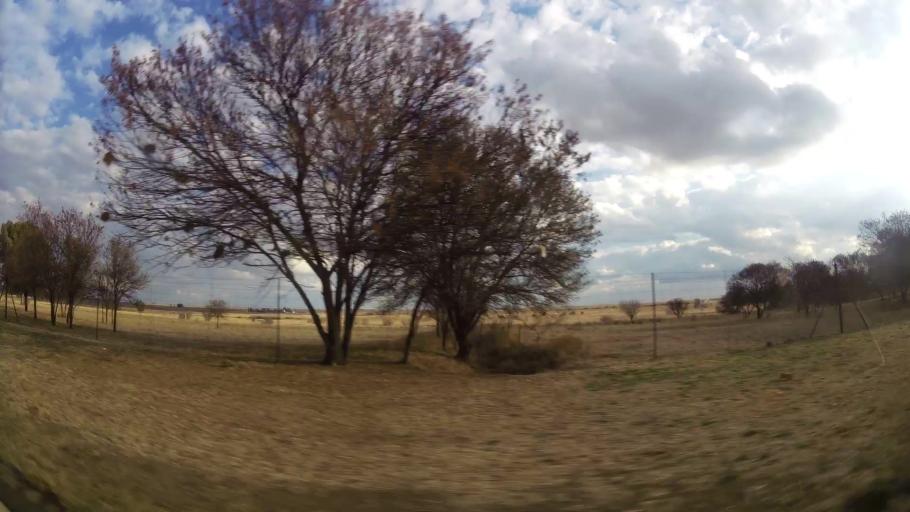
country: ZA
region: Orange Free State
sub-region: Fezile Dabi District Municipality
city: Sasolburg
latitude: -26.8230
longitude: 27.8107
